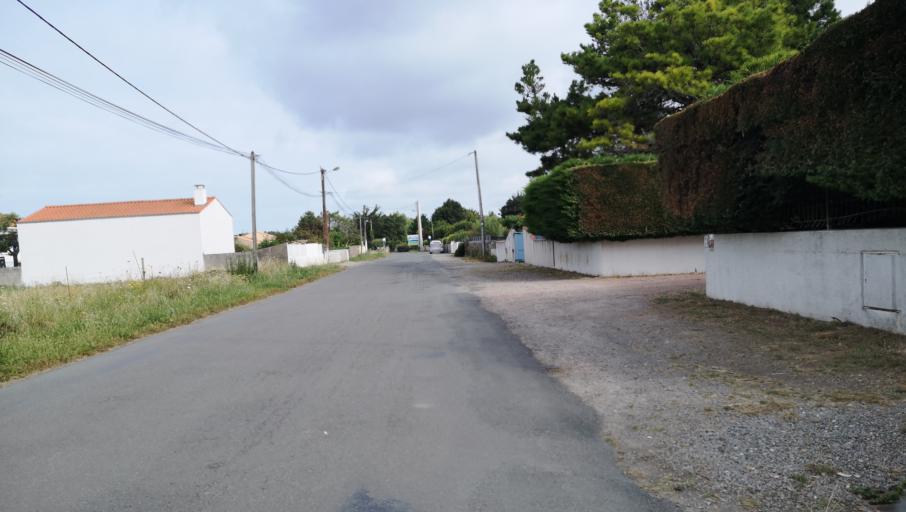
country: FR
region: Pays de la Loire
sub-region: Departement de la Vendee
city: Olonne-sur-Mer
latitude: 46.5531
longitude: -1.8048
